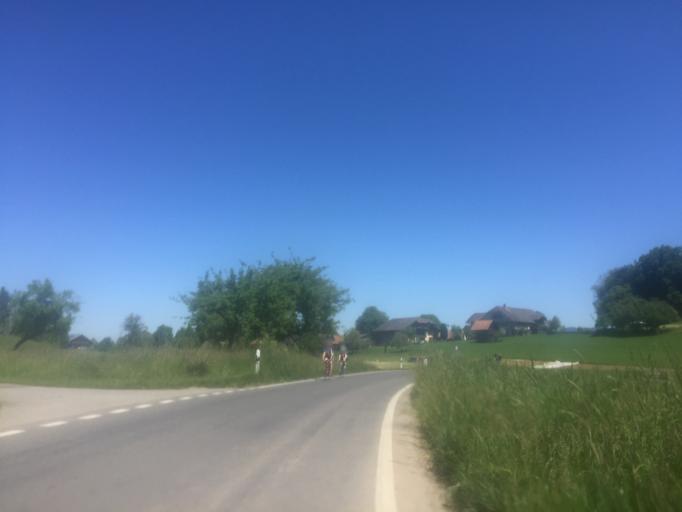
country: CH
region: Bern
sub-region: Thun District
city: Thierachern
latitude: 46.7480
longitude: 7.5648
